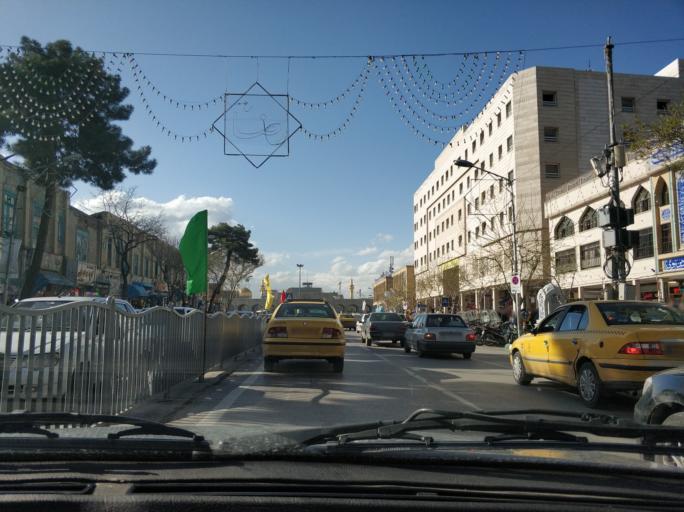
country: IR
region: Razavi Khorasan
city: Mashhad
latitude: 36.2849
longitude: 59.6201
